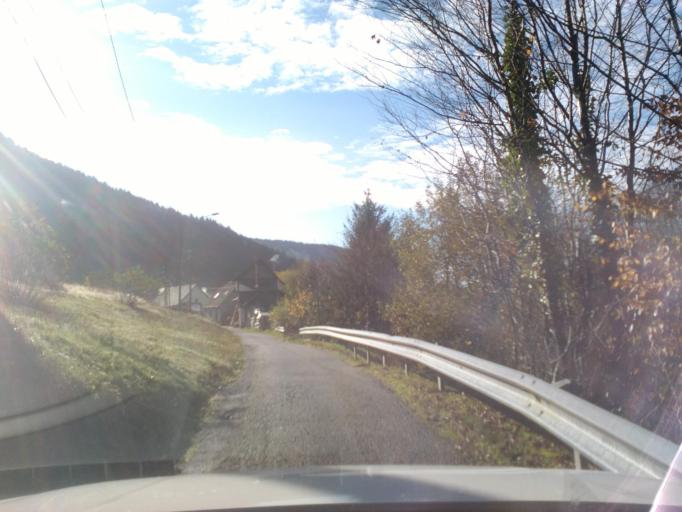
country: FR
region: Lorraine
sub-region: Departement des Vosges
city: Senones
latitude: 48.4390
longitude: 7.0361
